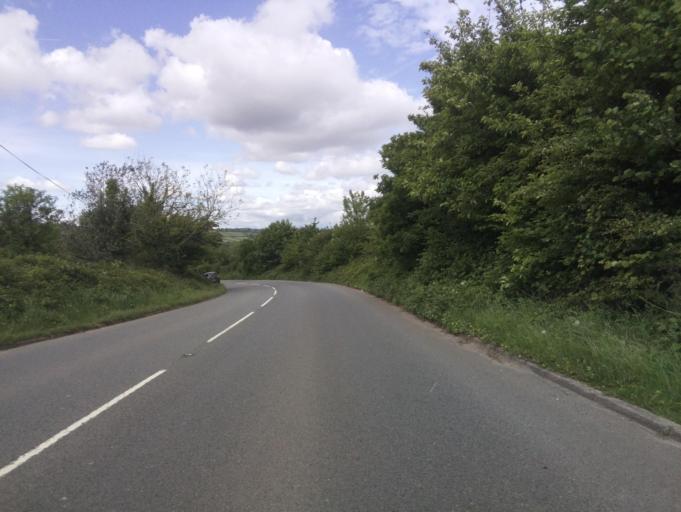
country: GB
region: England
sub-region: Devon
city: South Brent
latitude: 50.4040
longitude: -3.8506
